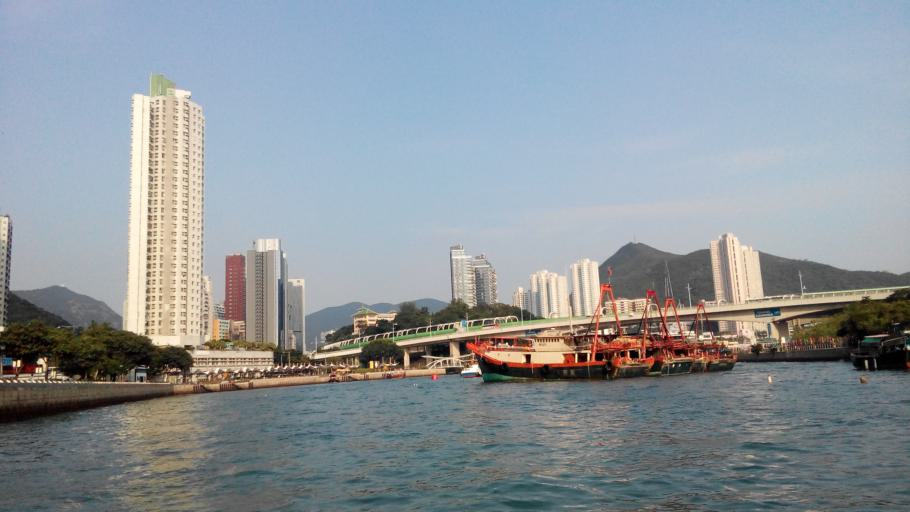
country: HK
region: Central and Western
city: Central
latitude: 22.2465
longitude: 114.1563
